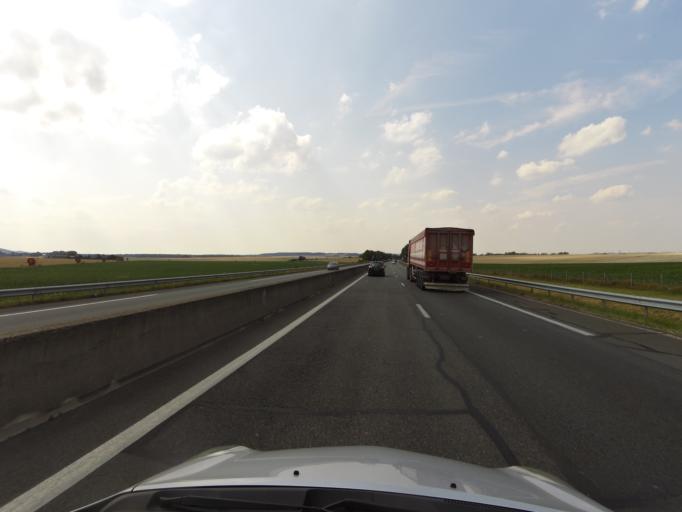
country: FR
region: Picardie
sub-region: Departement de l'Aisne
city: Couvron-et-Aumencourt
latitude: 49.6600
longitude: 3.5483
